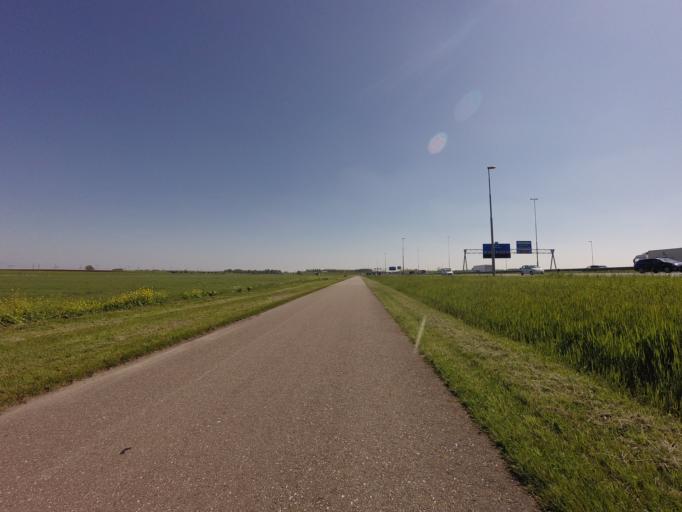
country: NL
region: South Holland
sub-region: Gemeente Strijen
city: Strijen
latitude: 51.7077
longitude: 4.6438
